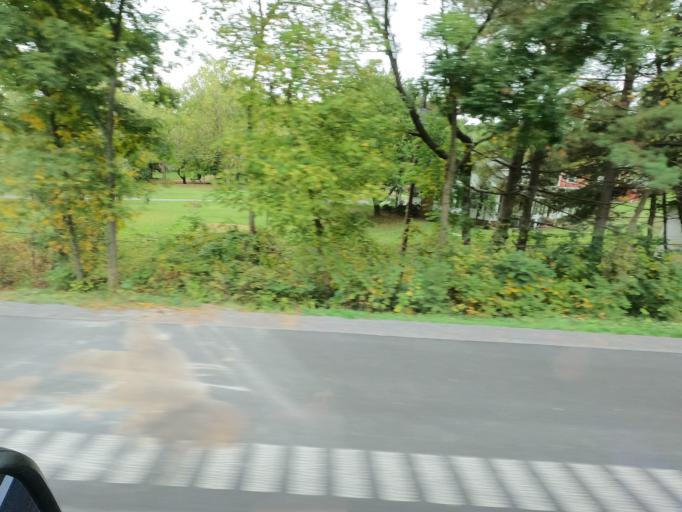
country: US
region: Tennessee
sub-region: Sullivan County
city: Colonial Heights
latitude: 36.5340
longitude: -82.5031
